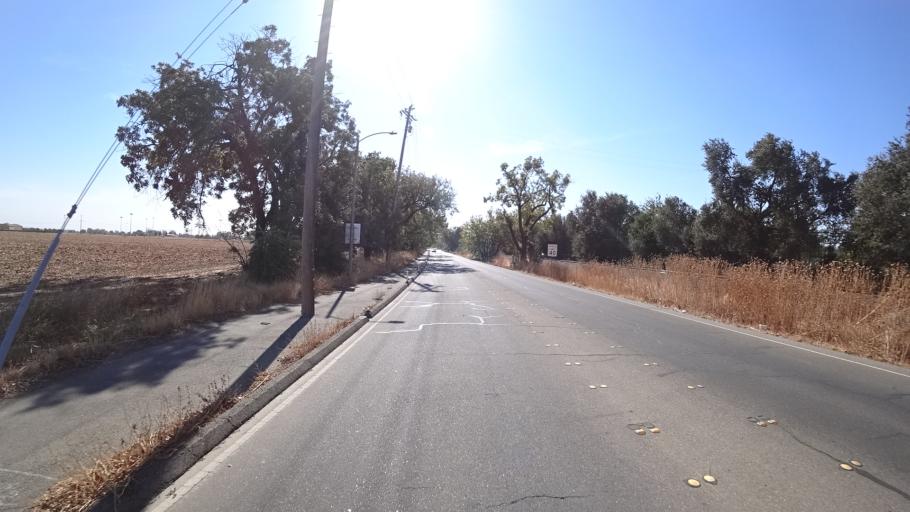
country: US
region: California
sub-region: Yolo County
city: Woodland
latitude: 38.6586
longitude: -121.7657
